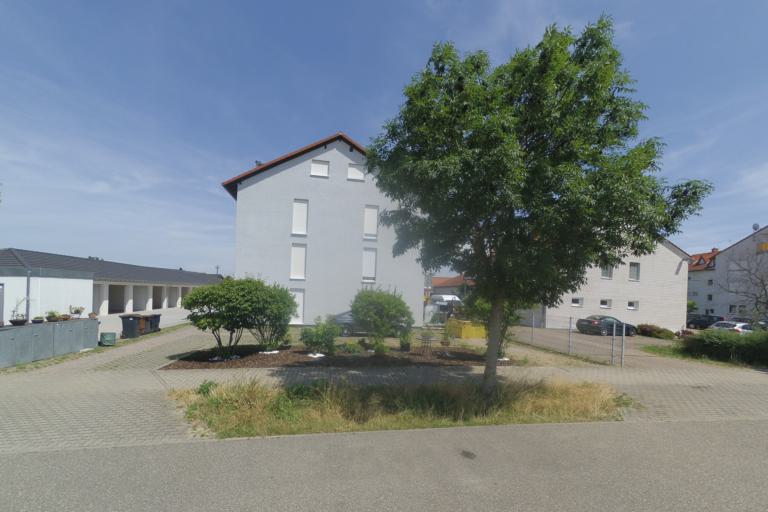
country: DE
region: Rheinland-Pfalz
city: Limburgerhof
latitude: 49.4272
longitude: 8.3897
